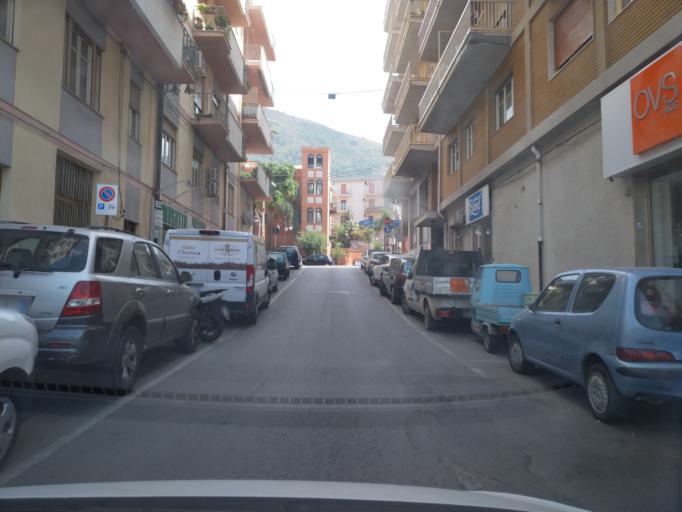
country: IT
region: Sicily
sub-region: Palermo
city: Cefalu
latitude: 38.0336
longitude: 14.0157
